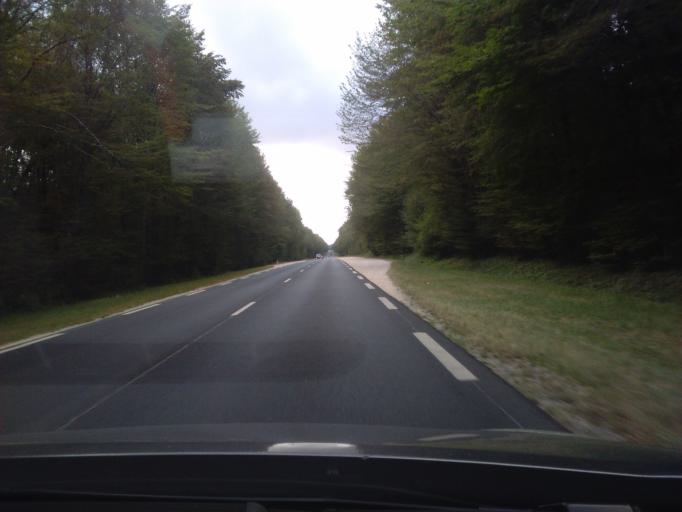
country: FR
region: Centre
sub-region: Departement du Loir-et-Cher
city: Cellettes
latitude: 47.5504
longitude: 1.3739
